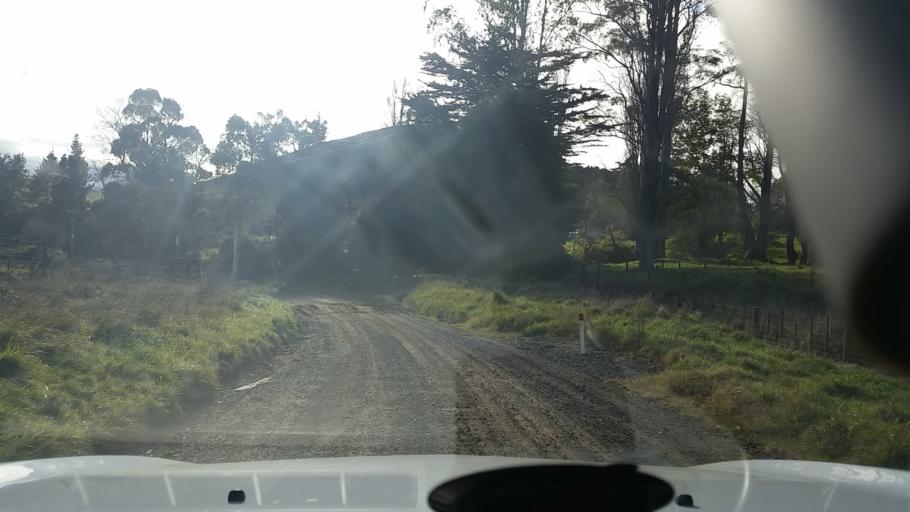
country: NZ
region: Hawke's Bay
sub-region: Napier City
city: Napier
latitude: -39.2414
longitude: 176.8154
